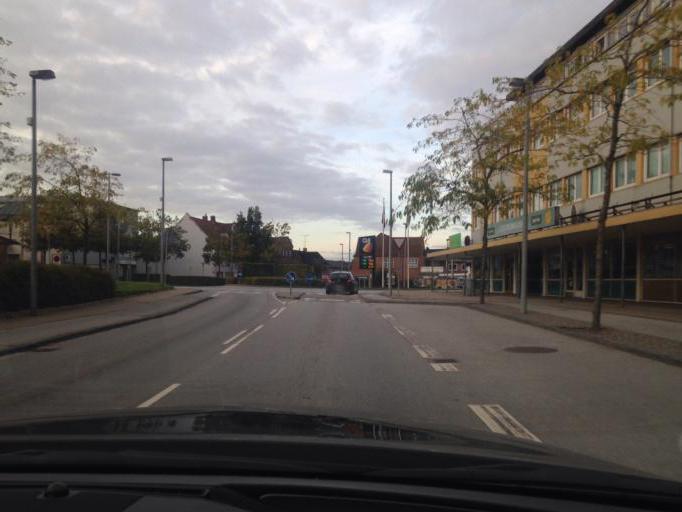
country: DK
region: South Denmark
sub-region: Haderslev Kommune
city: Vojens
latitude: 55.2468
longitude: 9.3035
